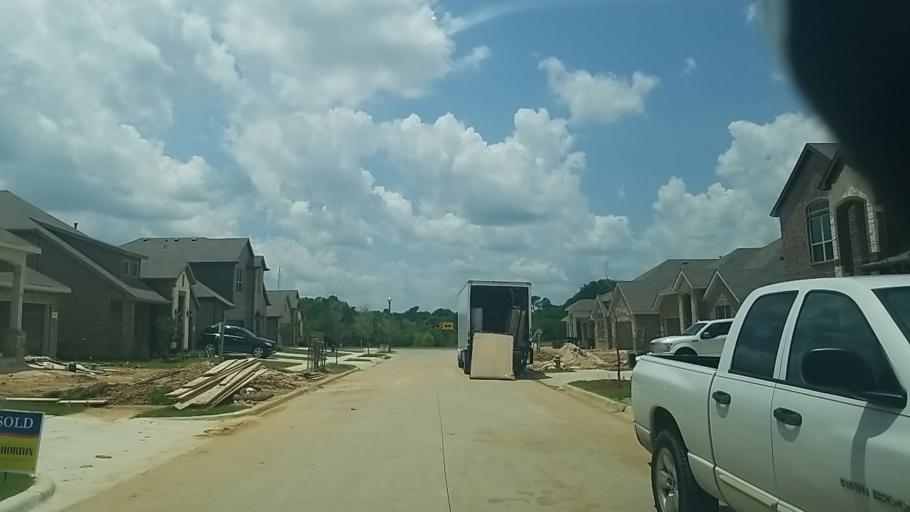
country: US
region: Texas
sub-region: Denton County
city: Denton
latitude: 33.1685
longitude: -97.1155
